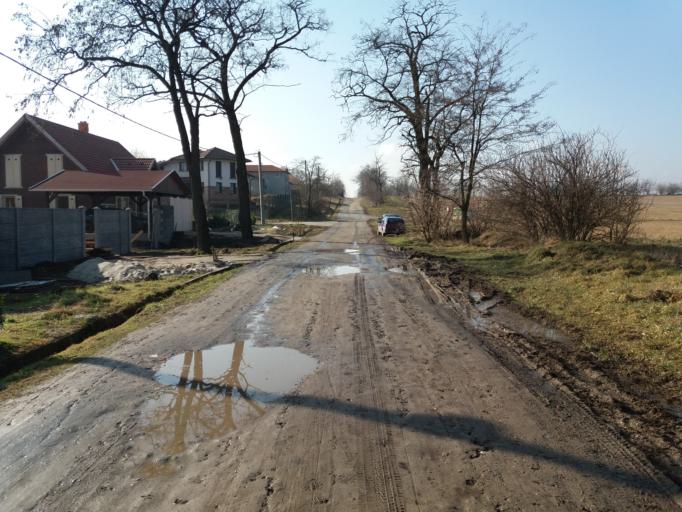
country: HU
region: Pest
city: Paty
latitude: 47.5180
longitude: 18.8091
